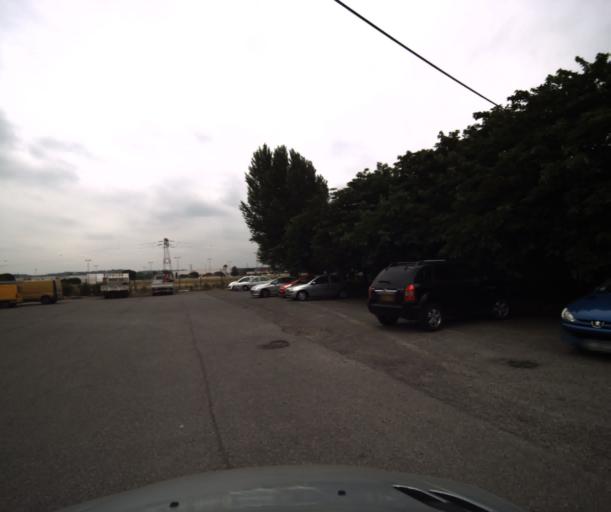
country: FR
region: Midi-Pyrenees
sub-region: Departement de la Haute-Garonne
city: Portet-sur-Garonne
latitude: 43.5378
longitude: 1.4003
